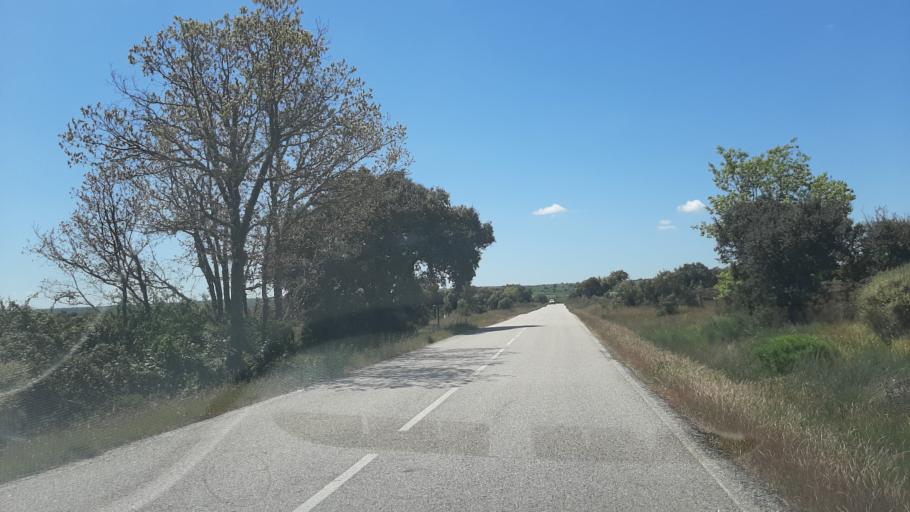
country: ES
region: Castille and Leon
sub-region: Provincia de Salamanca
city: Villarmuerto
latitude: 41.0410
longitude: -6.3916
